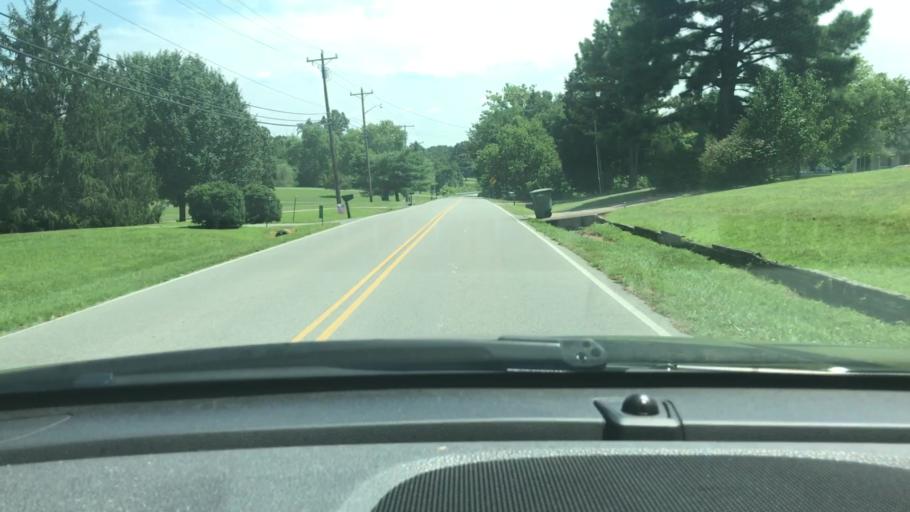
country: US
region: Tennessee
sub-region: Sumner County
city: White House
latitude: 36.4631
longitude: -86.6475
